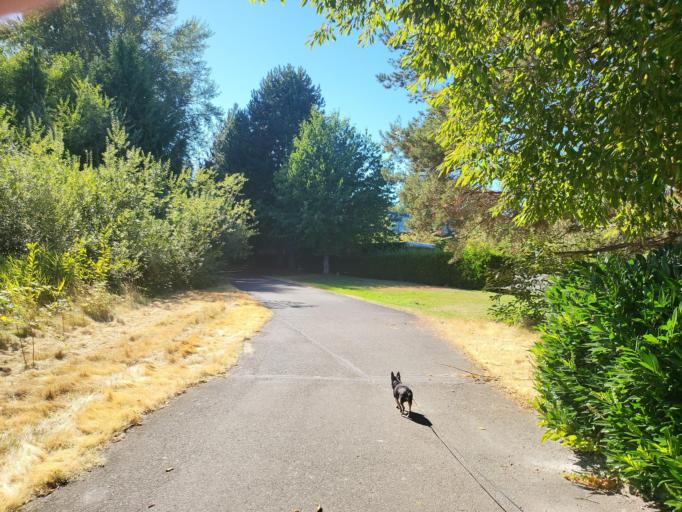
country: US
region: Washington
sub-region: King County
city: Tukwila
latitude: 47.4669
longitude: -122.2458
